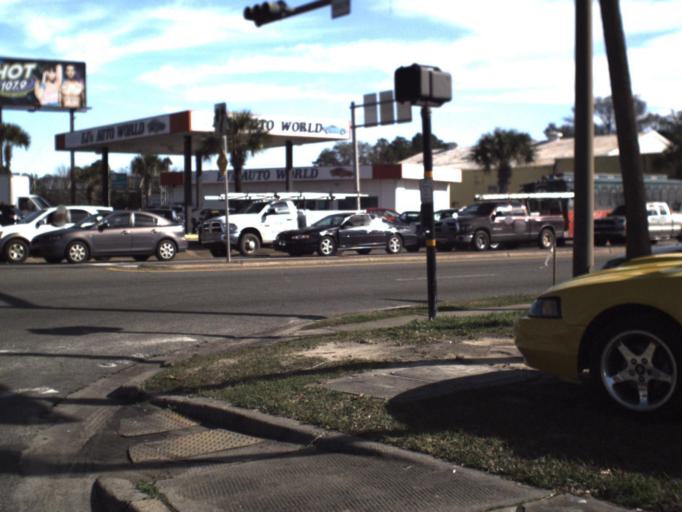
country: US
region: Florida
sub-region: Bay County
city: Panama City
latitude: 30.1749
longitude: -85.6601
